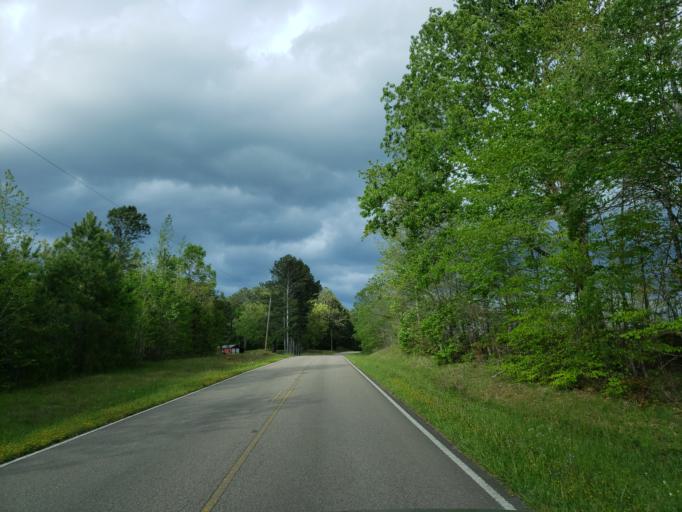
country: US
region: Georgia
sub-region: Haralson County
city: Tallapoosa
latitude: 33.8486
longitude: -85.3831
